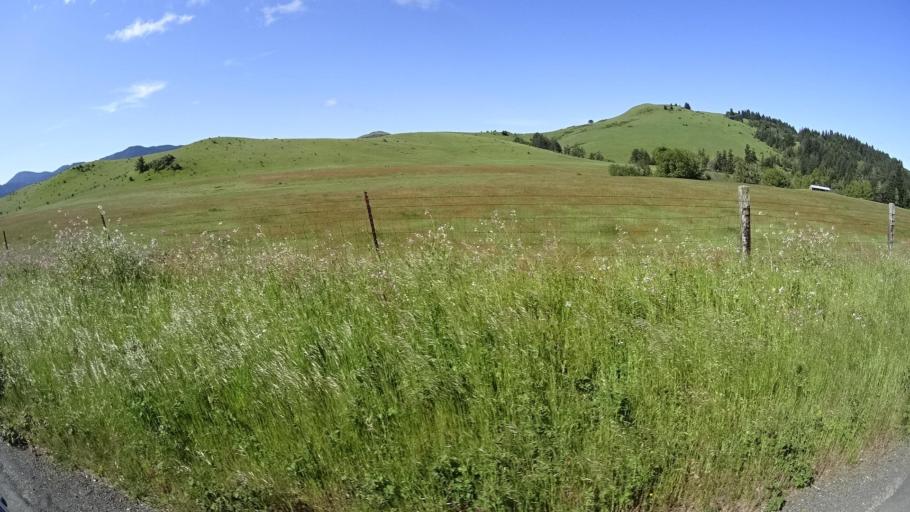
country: US
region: California
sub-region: Humboldt County
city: Ferndale
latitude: 40.3398
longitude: -124.3149
